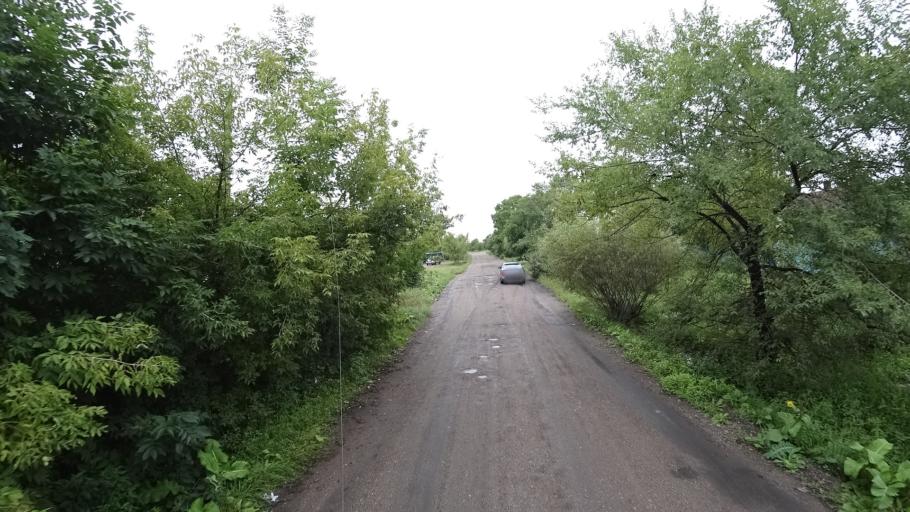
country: RU
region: Primorskiy
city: Monastyrishche
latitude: 44.1974
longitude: 132.4645
